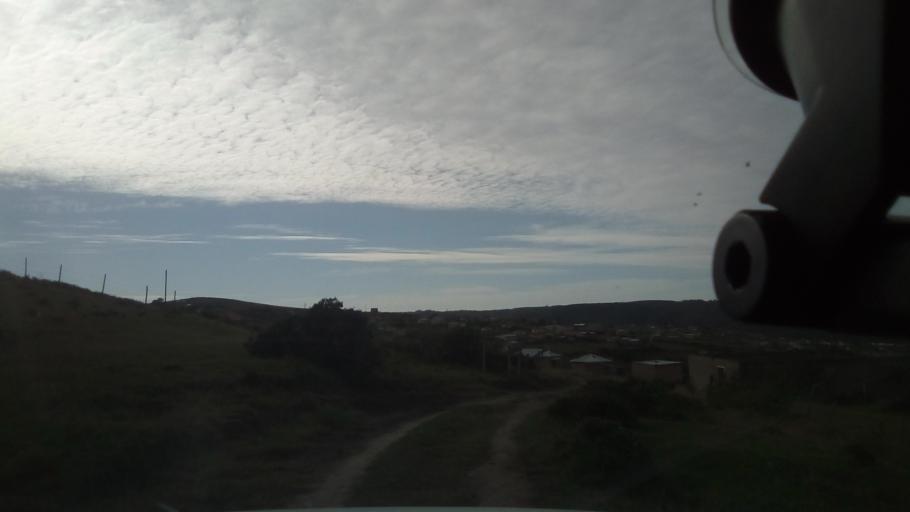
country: ZA
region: Eastern Cape
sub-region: Buffalo City Metropolitan Municipality
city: East London
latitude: -32.8010
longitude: 27.9648
